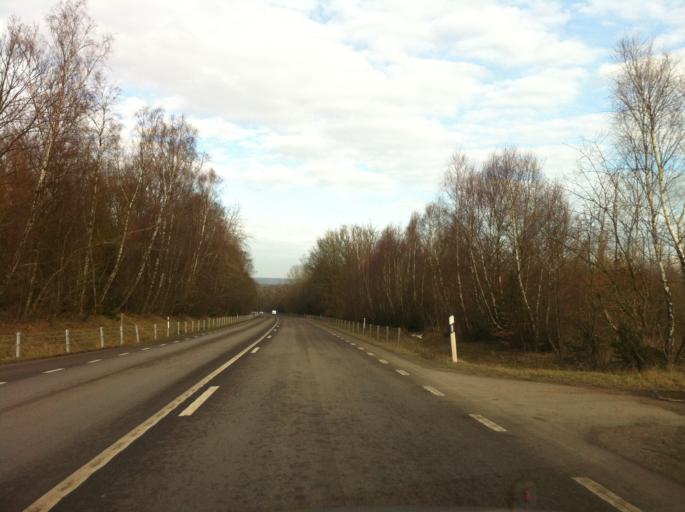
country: SE
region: Skane
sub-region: Bjuvs Kommun
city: Billesholm
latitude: 56.0339
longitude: 12.9692
